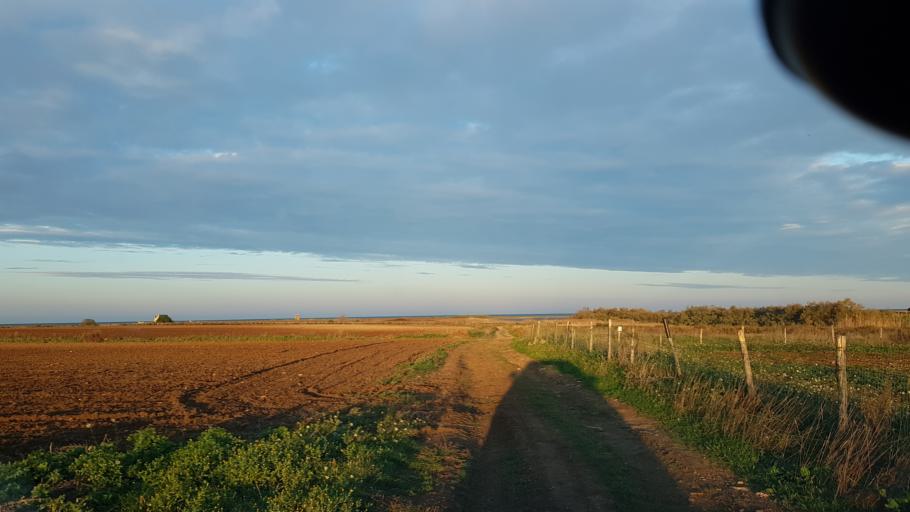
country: IT
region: Apulia
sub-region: Provincia di Brindisi
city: La Rosa
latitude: 40.6112
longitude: 18.0164
